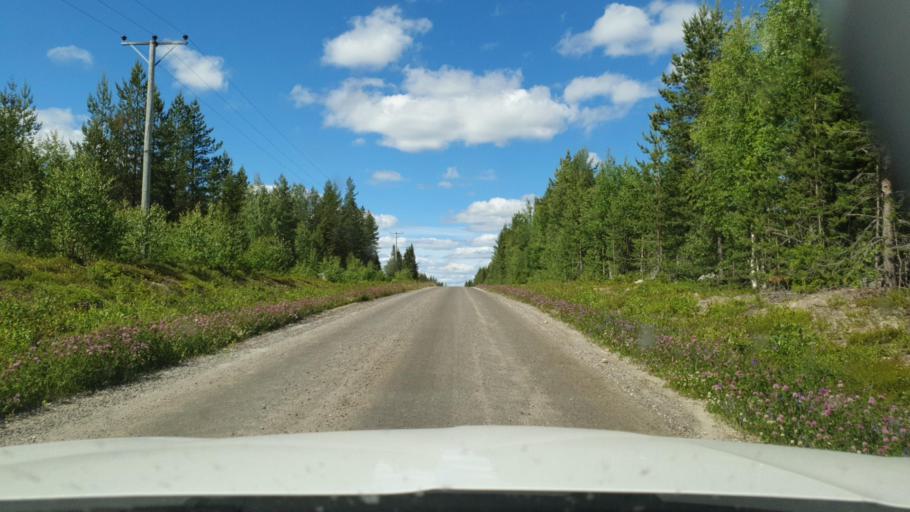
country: SE
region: Vaesterbotten
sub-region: Skelleftea Kommun
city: Backa
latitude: 65.1736
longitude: 21.0990
